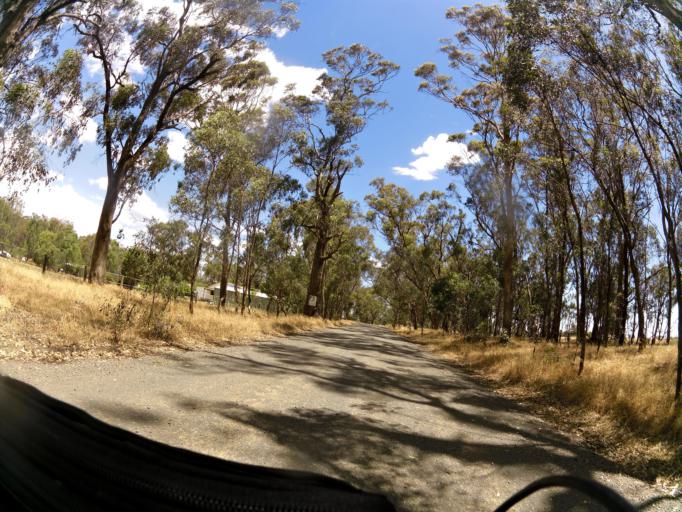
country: AU
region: Victoria
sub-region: Campaspe
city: Kyabram
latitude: -36.7925
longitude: 145.0866
